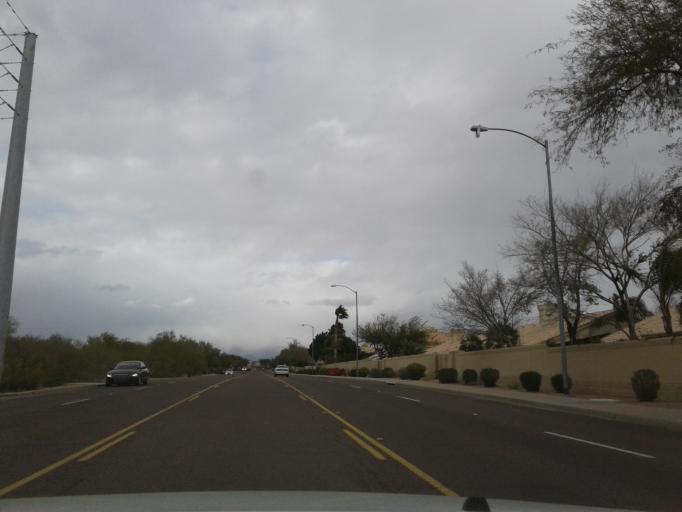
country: US
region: Arizona
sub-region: Maricopa County
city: Paradise Valley
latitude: 33.6212
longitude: -111.8870
